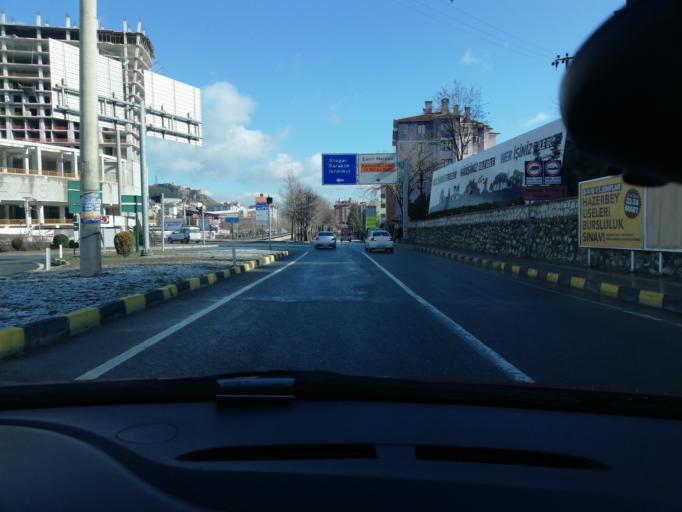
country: TR
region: Kastamonu
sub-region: Cide
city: Kastamonu
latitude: 41.3626
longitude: 33.7671
